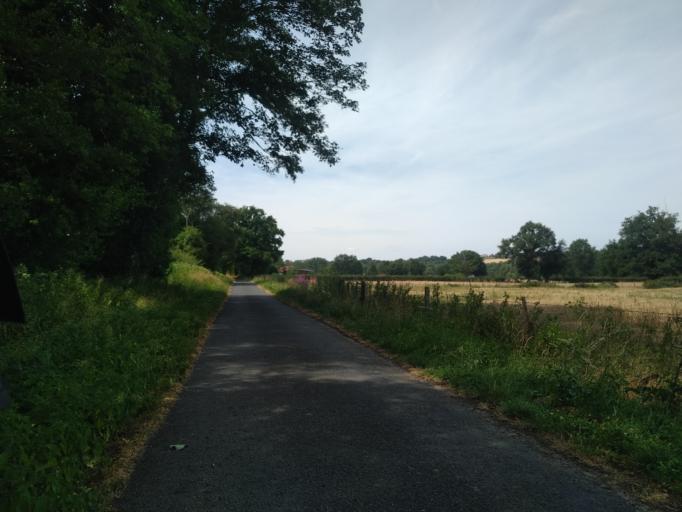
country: FR
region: Auvergne
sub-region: Departement de l'Allier
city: Diou
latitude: 46.5297
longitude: 3.7711
